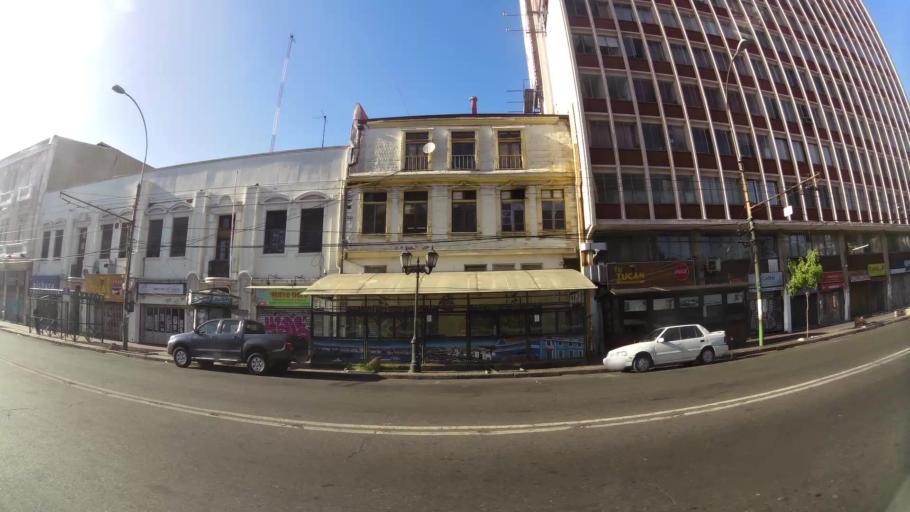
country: CL
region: Valparaiso
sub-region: Provincia de Valparaiso
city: Valparaiso
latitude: -33.0466
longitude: -71.6189
